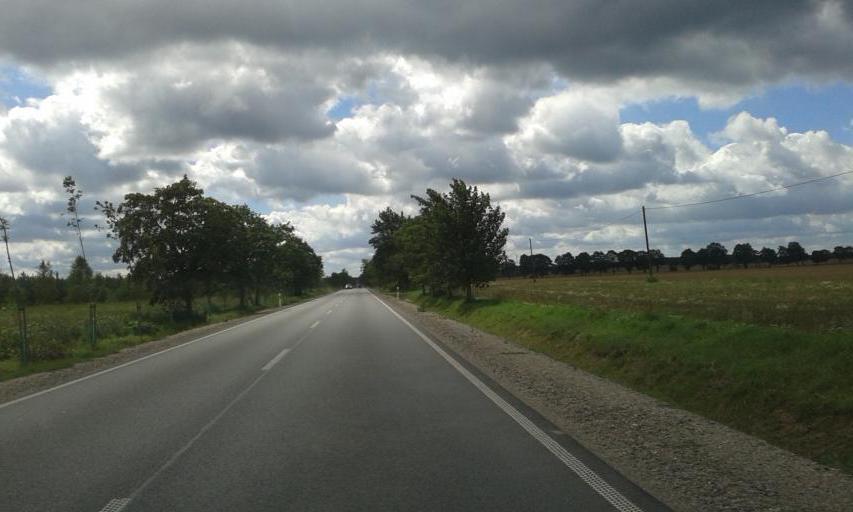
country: PL
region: West Pomeranian Voivodeship
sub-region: Powiat szczecinecki
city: Lubowo
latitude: 53.4994
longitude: 16.3309
